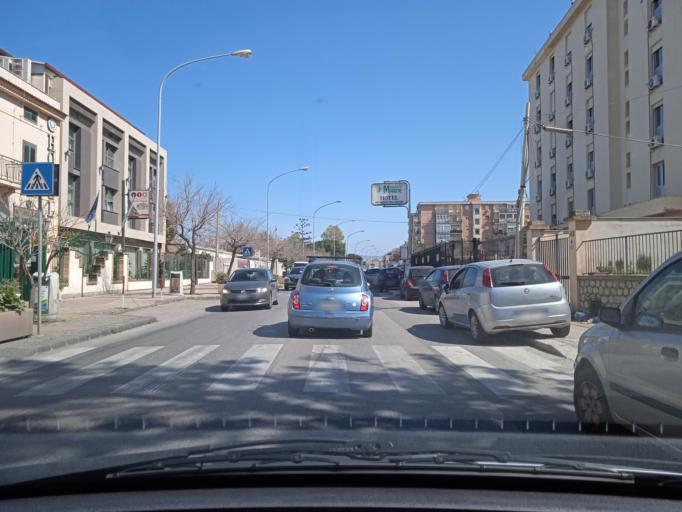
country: IT
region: Sicily
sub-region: Palermo
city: Ciaculli
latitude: 38.1018
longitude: 13.3977
